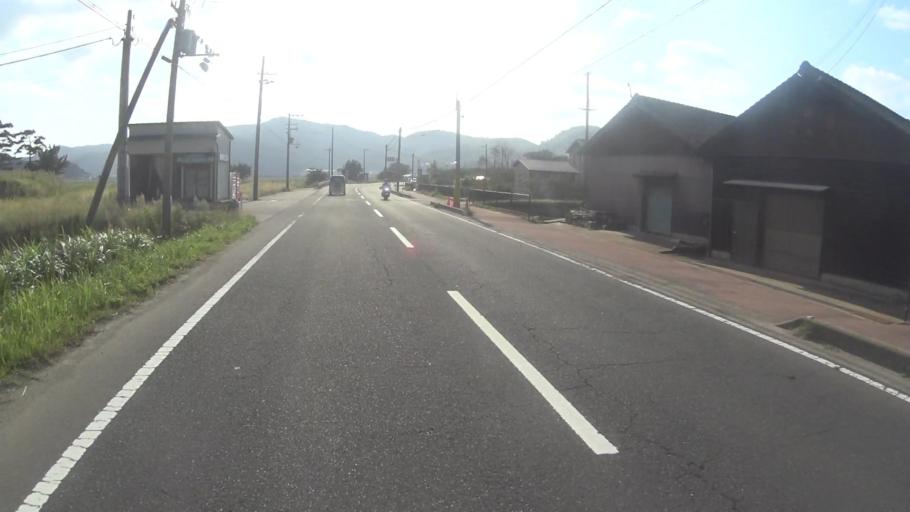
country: JP
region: Kyoto
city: Miyazu
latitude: 35.7390
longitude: 135.1087
